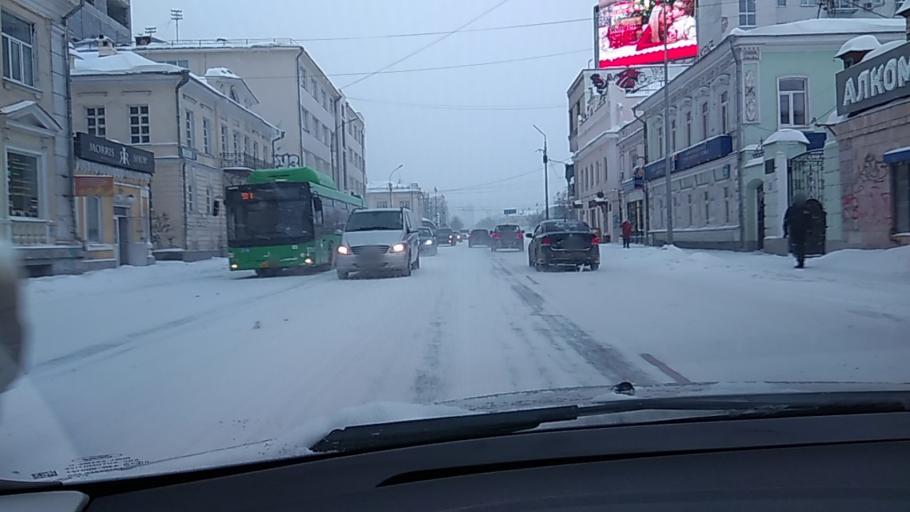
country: RU
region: Sverdlovsk
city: Yekaterinburg
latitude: 56.8329
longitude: 60.6003
